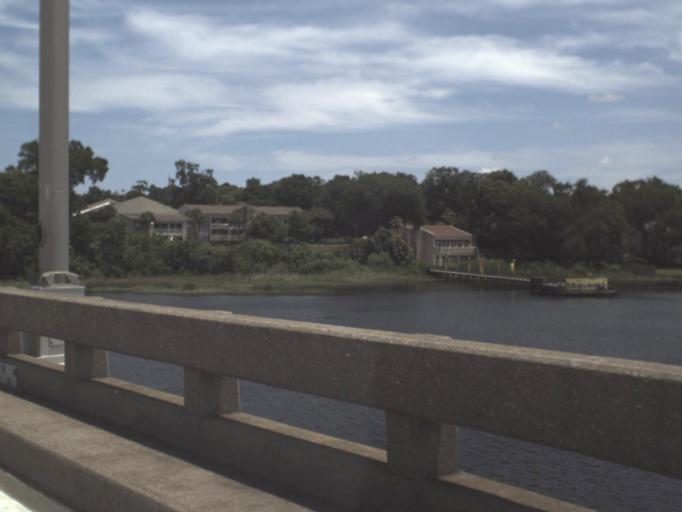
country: US
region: Florida
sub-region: Duval County
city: Jacksonville
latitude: 30.3272
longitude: -81.6127
